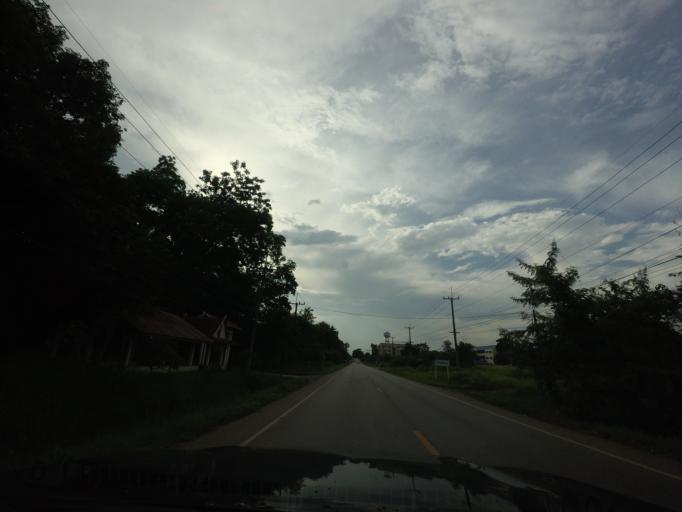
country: TH
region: Changwat Udon Thani
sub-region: Amphoe Ban Phue
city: Ban Phue
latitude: 17.7014
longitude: 102.4400
